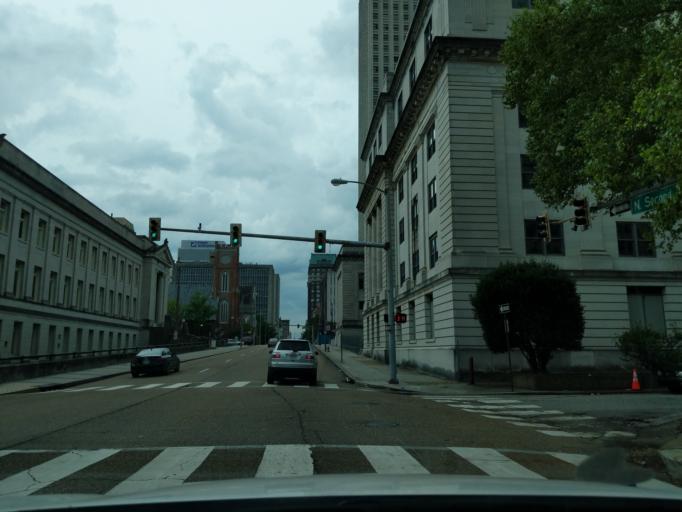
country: US
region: Tennessee
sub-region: Shelby County
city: Memphis
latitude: 35.1491
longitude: -90.0500
